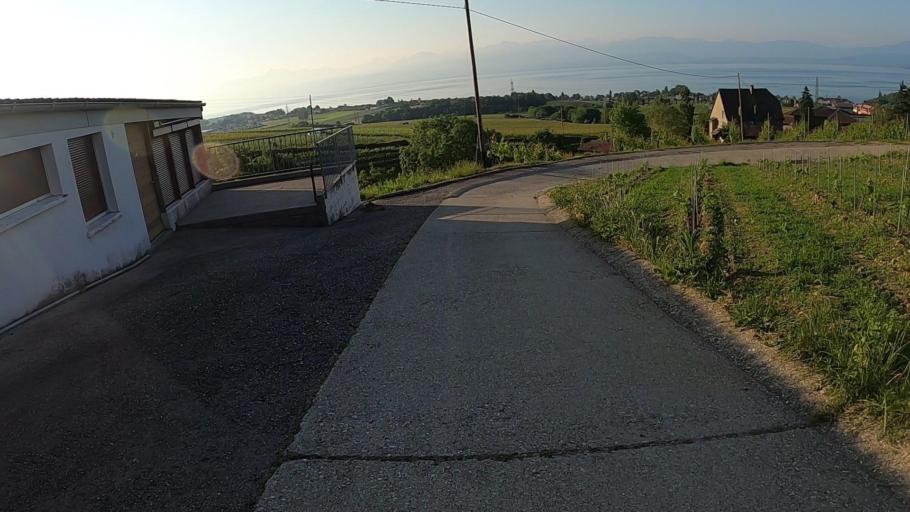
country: CH
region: Vaud
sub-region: Nyon District
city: Rolle
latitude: 46.4733
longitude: 6.3444
